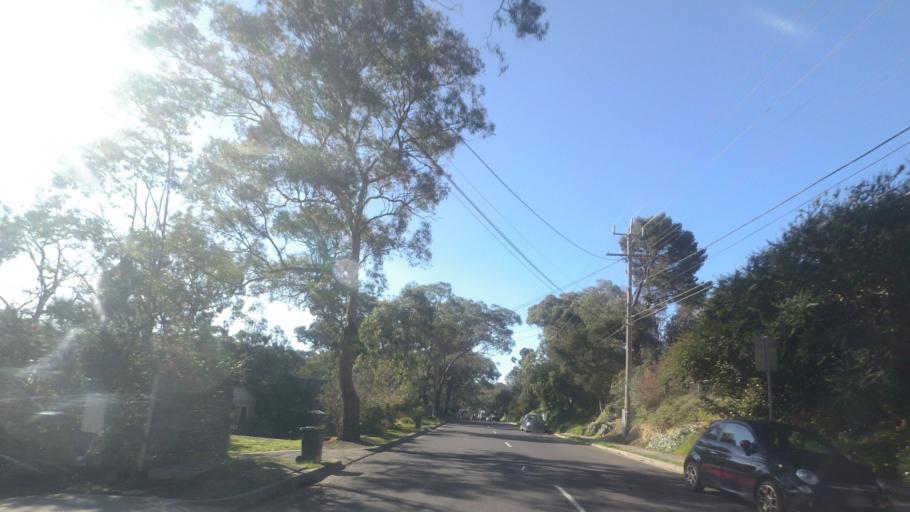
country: AU
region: Victoria
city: Saint Helena
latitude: -37.7166
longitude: 145.1334
